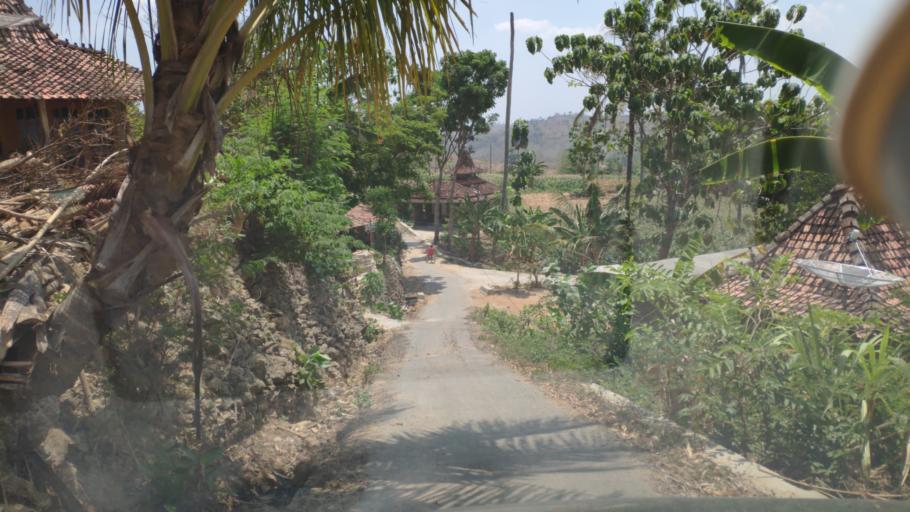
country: ID
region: Central Java
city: Guyangan
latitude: -6.9236
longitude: 111.1166
